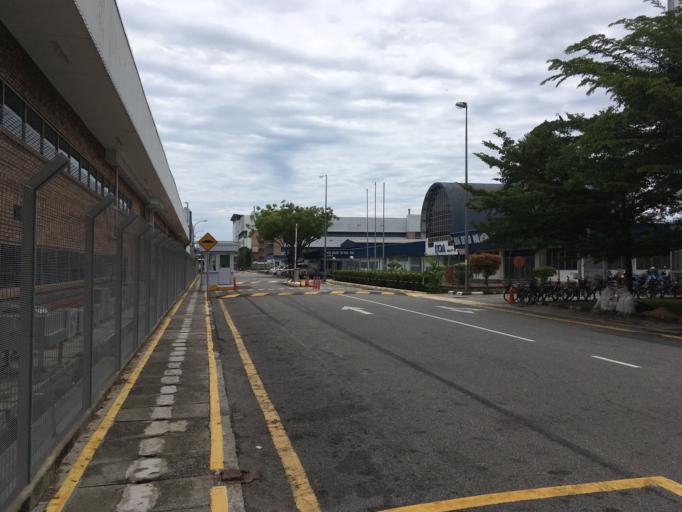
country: MY
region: Melaka
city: Batu Berendam
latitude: 2.2335
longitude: 102.2613
